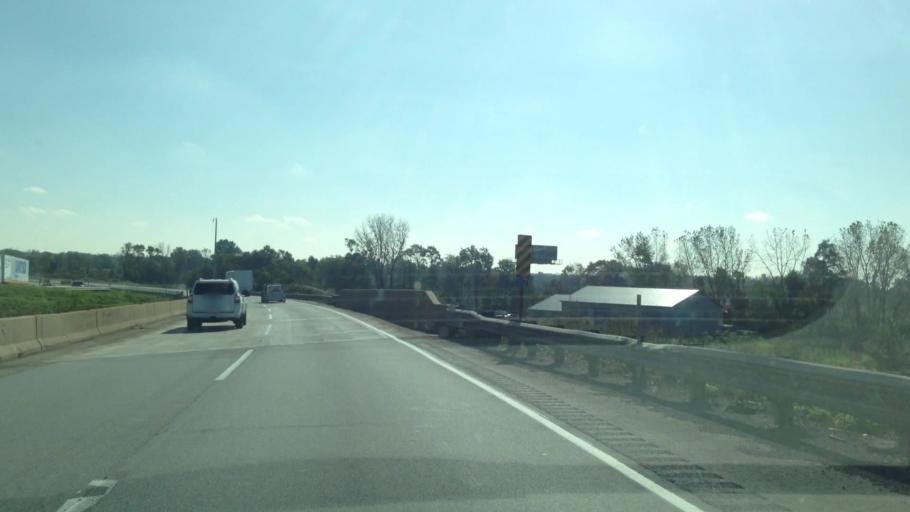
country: US
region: Indiana
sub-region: Porter County
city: Portage
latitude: 41.5737
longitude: -87.1538
